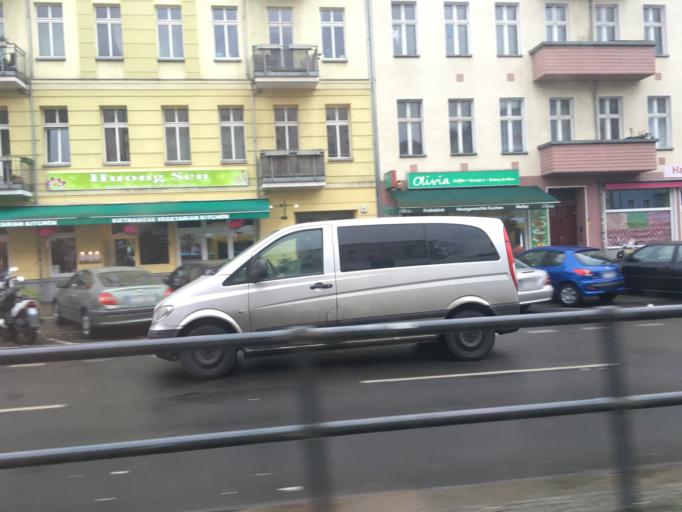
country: DE
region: Berlin
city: Prenzlauer Berg Bezirk
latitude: 52.5400
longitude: 13.4189
